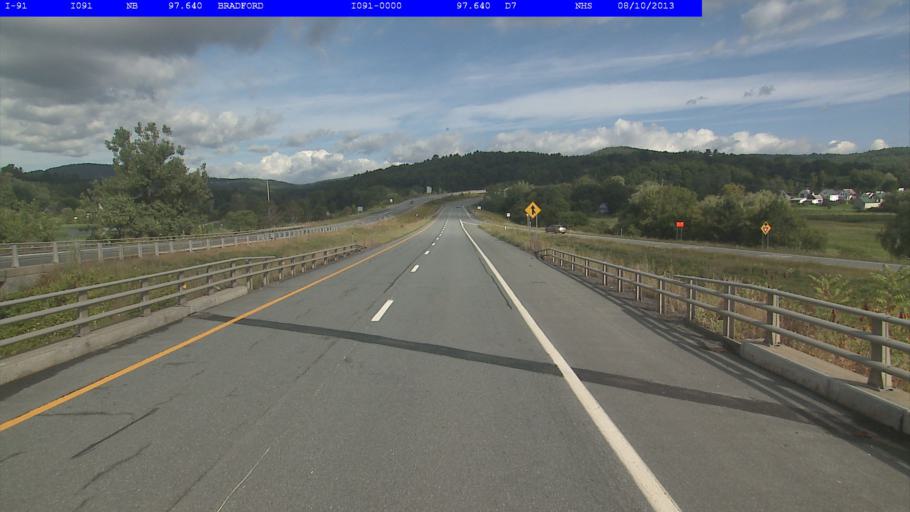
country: US
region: New Hampshire
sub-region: Grafton County
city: Orford
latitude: 43.9840
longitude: -72.1311
